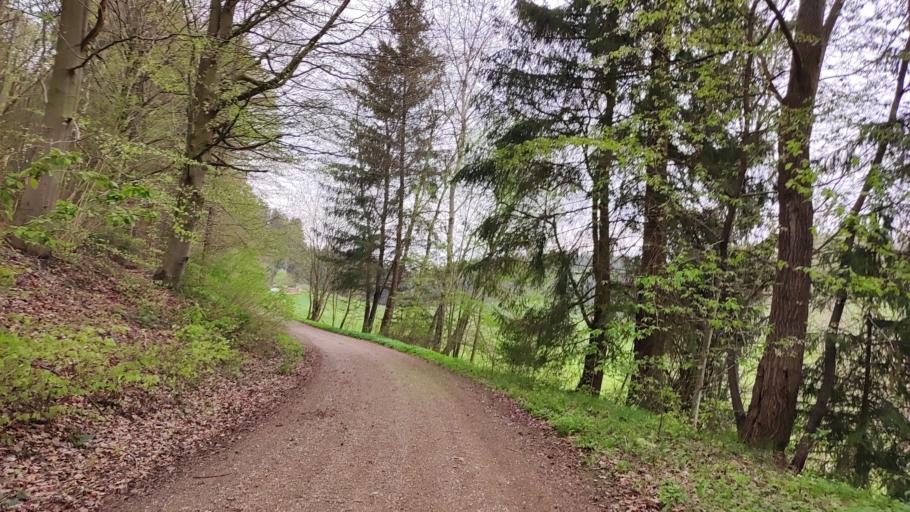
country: DE
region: Bavaria
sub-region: Swabia
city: Altenmunster
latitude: 48.4886
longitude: 10.5720
